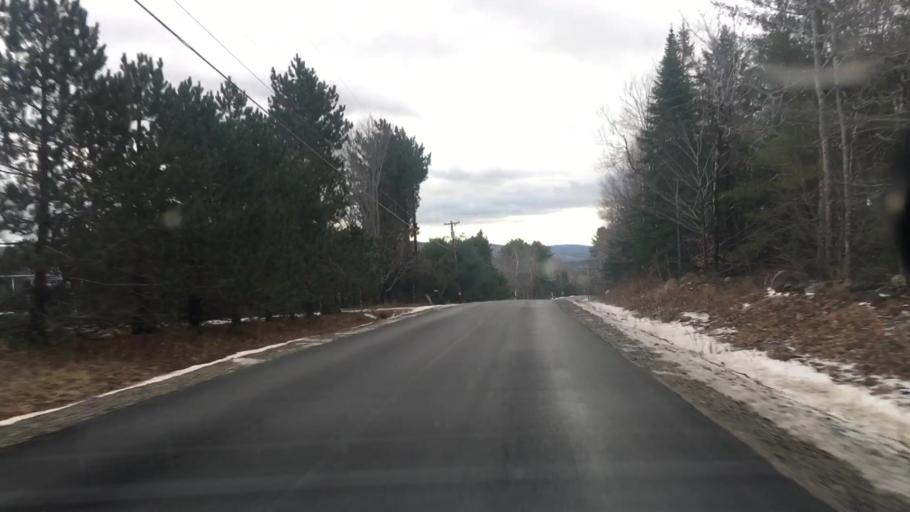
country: US
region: Maine
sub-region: Hancock County
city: Dedham
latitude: 44.6580
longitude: -68.7046
